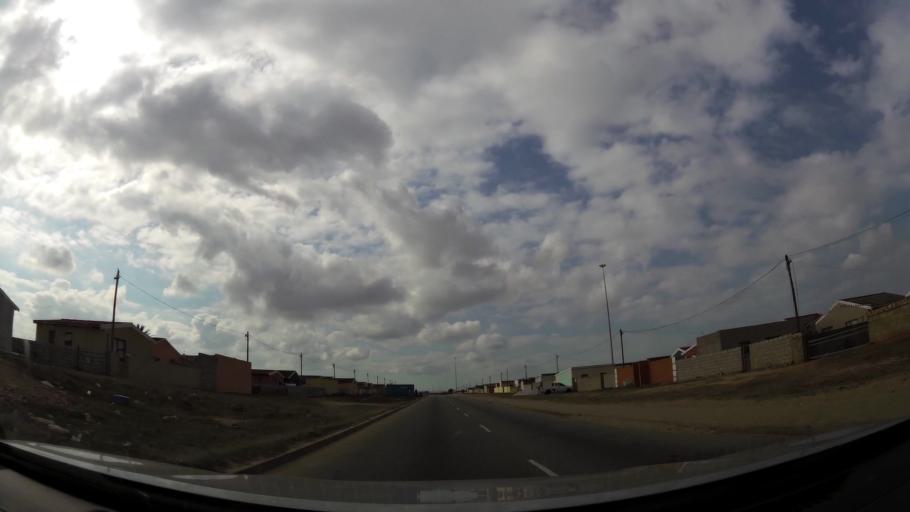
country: ZA
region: Eastern Cape
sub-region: Nelson Mandela Bay Metropolitan Municipality
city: Port Elizabeth
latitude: -33.8209
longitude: 25.5921
